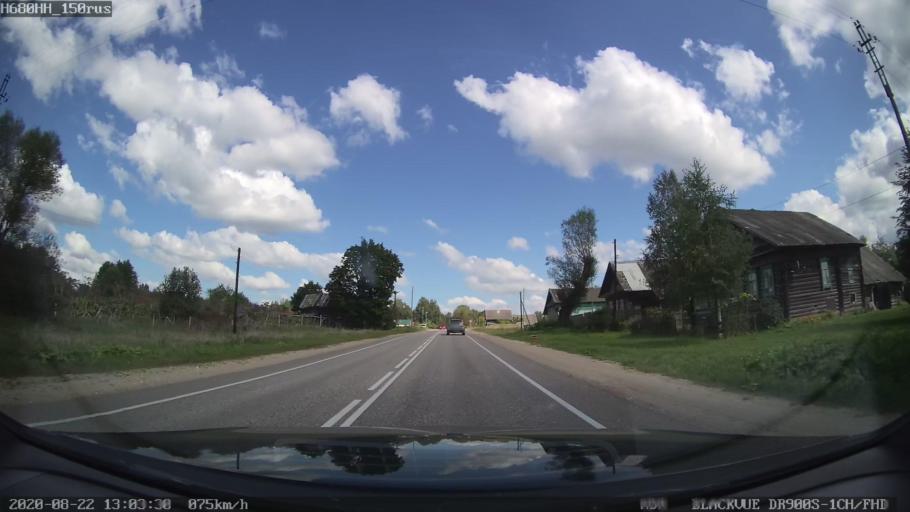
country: RU
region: Tverskaya
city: Bezhetsk
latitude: 57.6601
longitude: 36.4124
